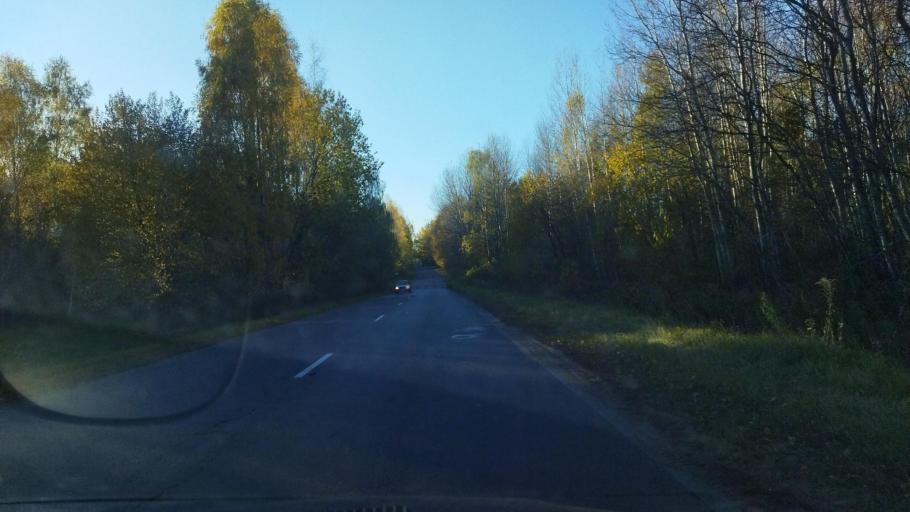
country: BY
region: Minsk
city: Kalodzishchy
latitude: 53.9466
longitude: 27.8270
